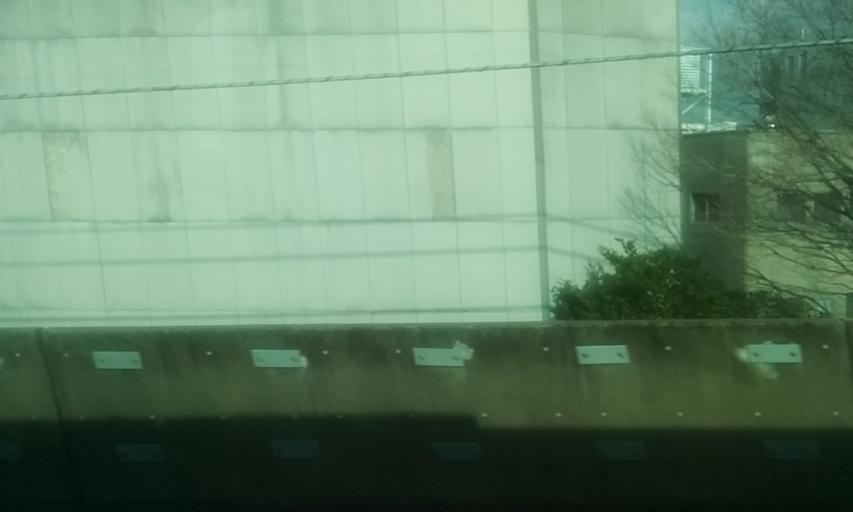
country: JP
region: Kanagawa
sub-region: Kawasaki-shi
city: Kawasaki
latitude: 35.5176
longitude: 139.6804
